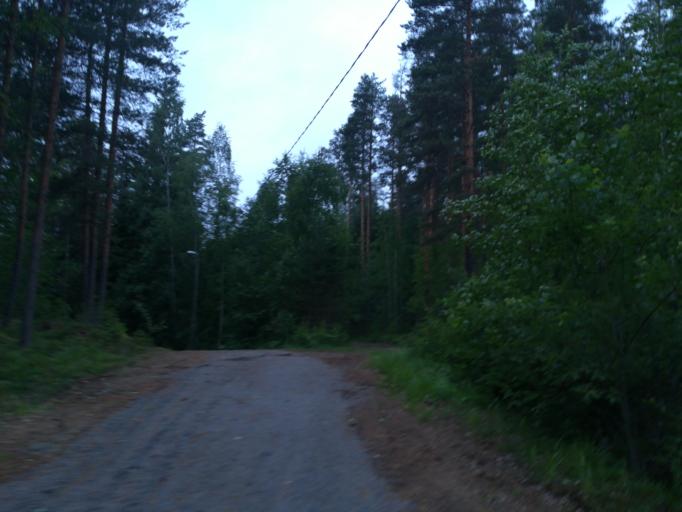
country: FI
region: Southern Savonia
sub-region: Mikkeli
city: Ristiina
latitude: 61.4839
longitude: 27.2855
